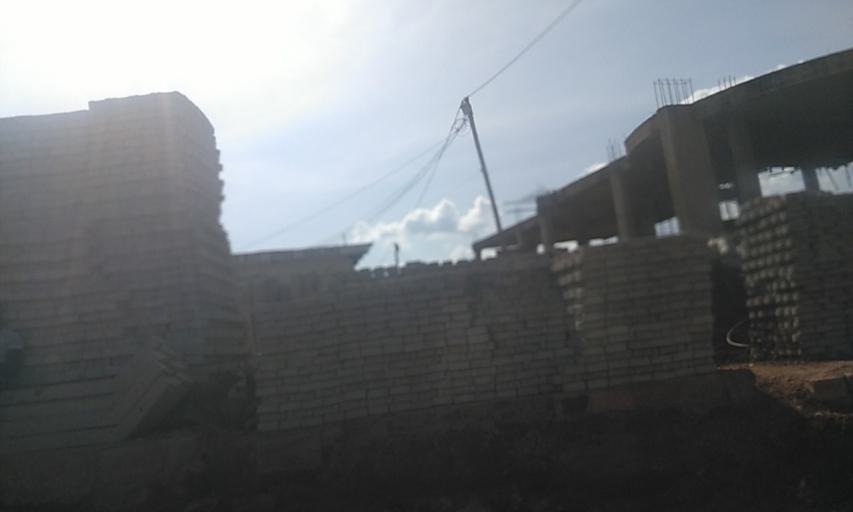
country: UG
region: Central Region
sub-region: Wakiso District
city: Kireka
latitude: 0.3856
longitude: 32.6258
